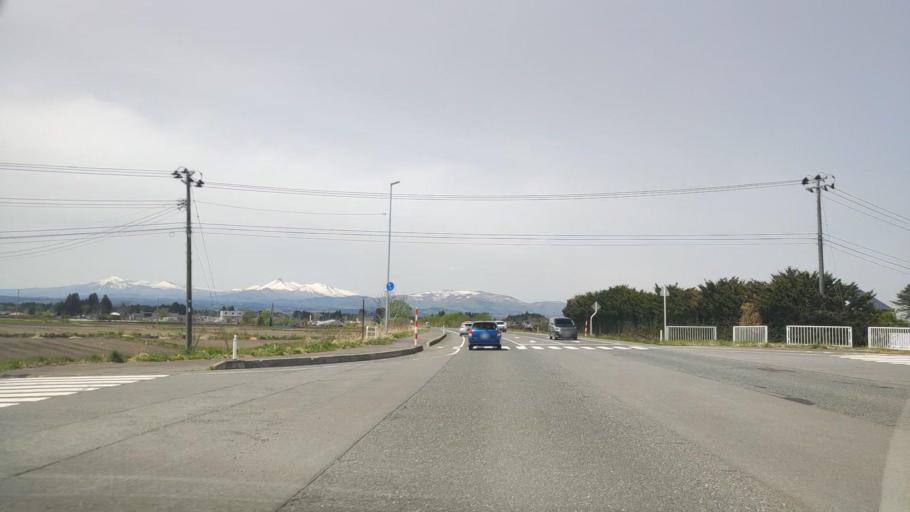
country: JP
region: Aomori
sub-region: Misawa Shi
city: Inuotose
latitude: 40.6384
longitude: 141.2383
